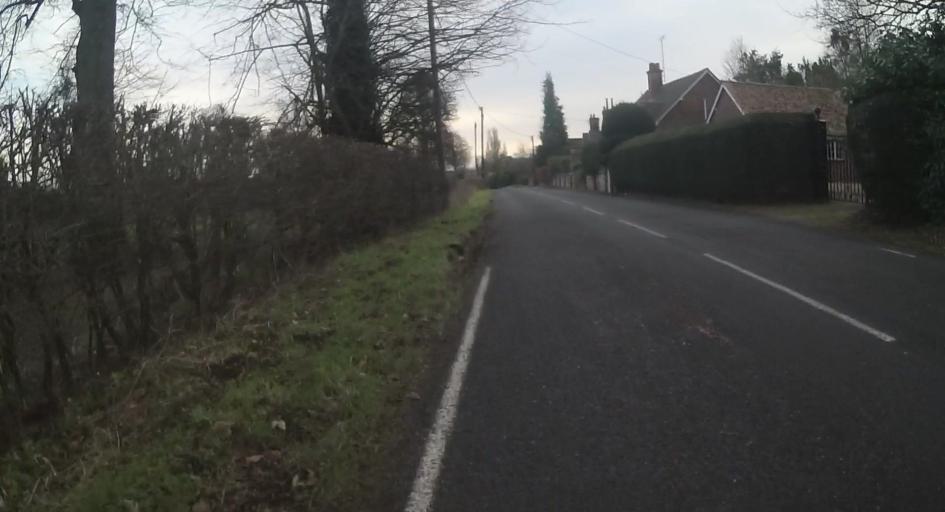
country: GB
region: England
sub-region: Hampshire
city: Overton
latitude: 51.2192
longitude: -1.3746
